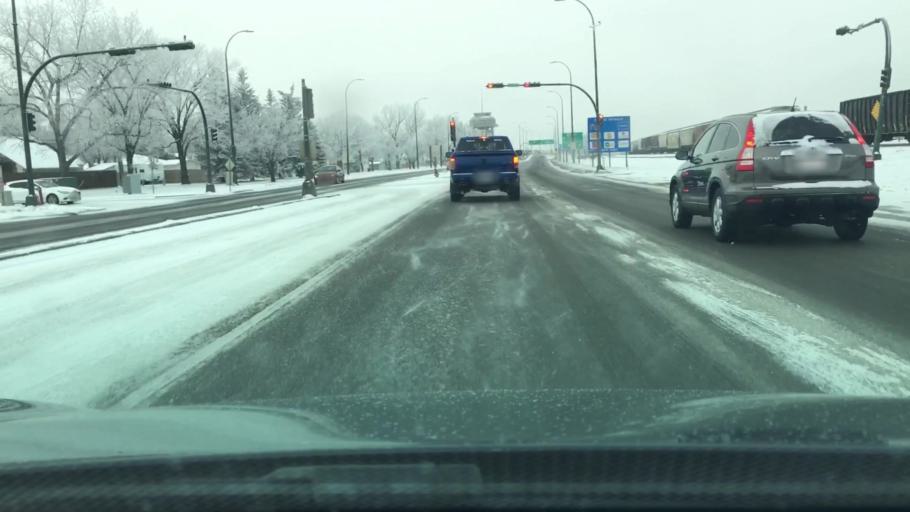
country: CA
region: Alberta
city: Lethbridge
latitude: 49.6981
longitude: -112.8009
